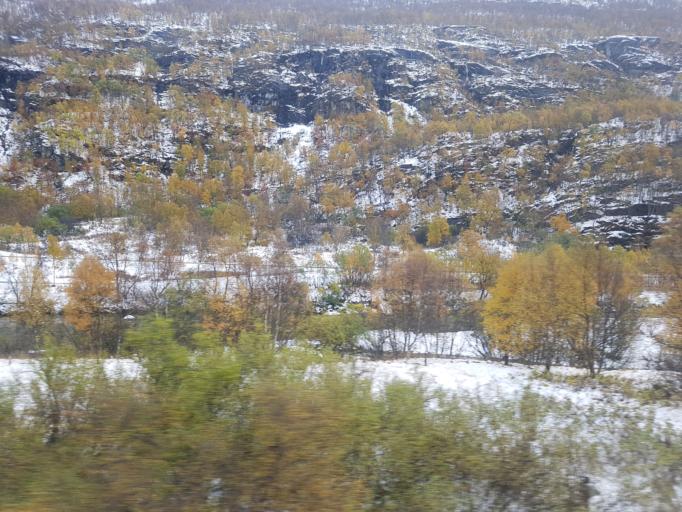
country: NO
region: Sor-Trondelag
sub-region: Oppdal
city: Oppdal
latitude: 62.4007
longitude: 9.6342
